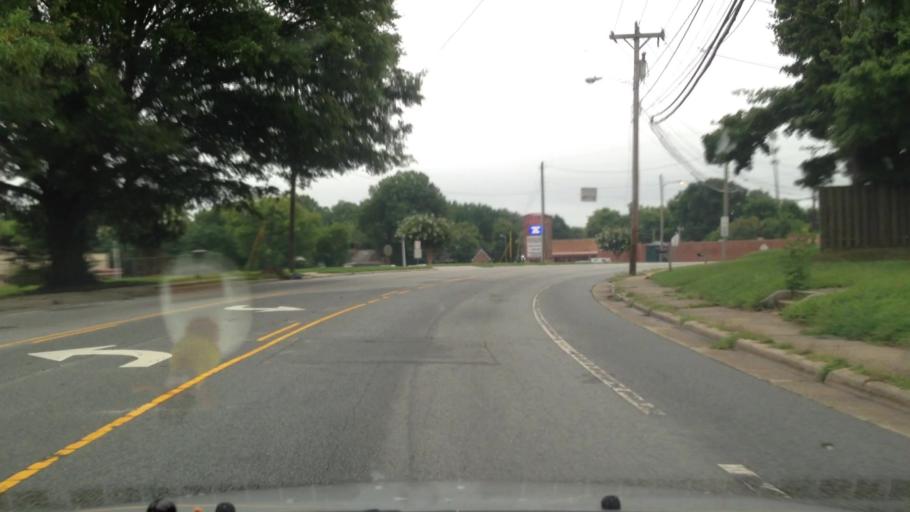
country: US
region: North Carolina
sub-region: Guilford County
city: Greensboro
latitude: 36.0484
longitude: -79.7756
